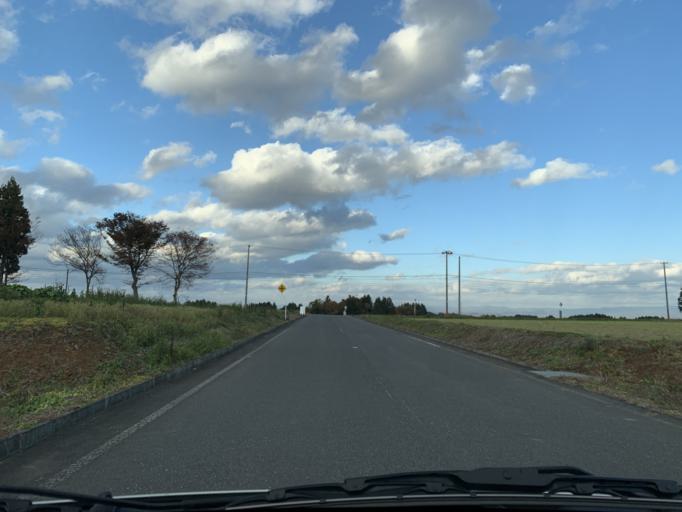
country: JP
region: Iwate
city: Mizusawa
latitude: 39.1066
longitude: 141.0226
